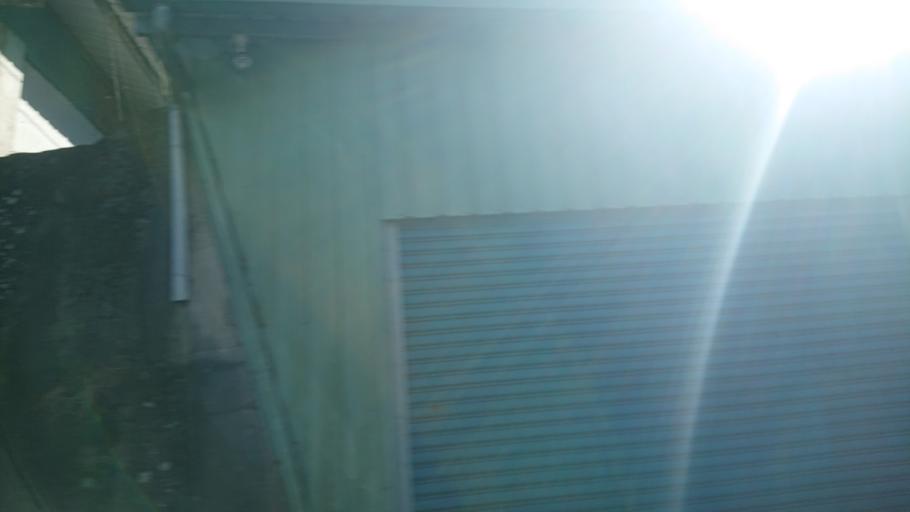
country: TW
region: Taiwan
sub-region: Chiayi
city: Jiayi Shi
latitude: 23.5207
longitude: 120.6305
